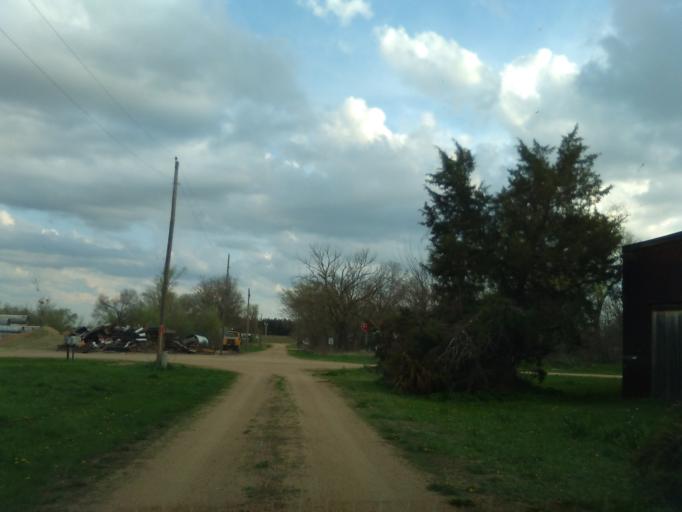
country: US
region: Nebraska
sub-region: Webster County
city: Red Cloud
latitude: 40.1719
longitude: -98.4490
